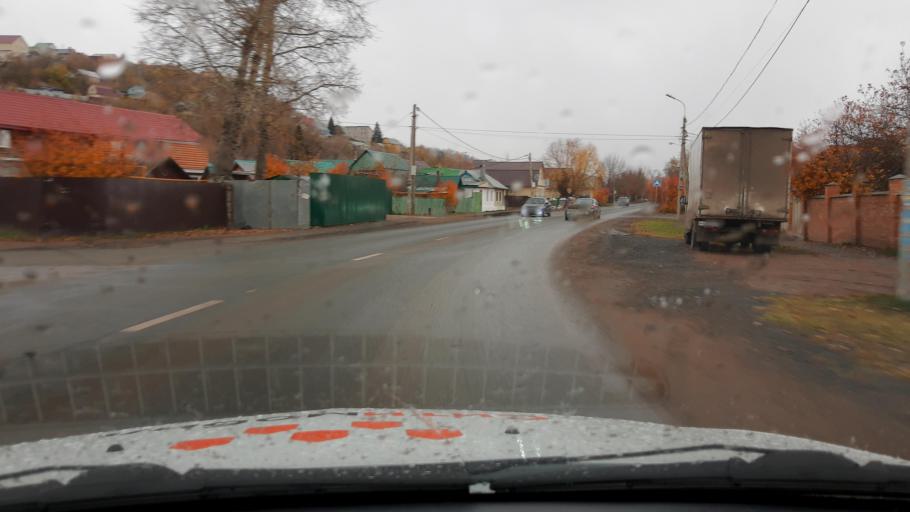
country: RU
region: Bashkortostan
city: Ufa
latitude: 54.7386
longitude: 55.9215
